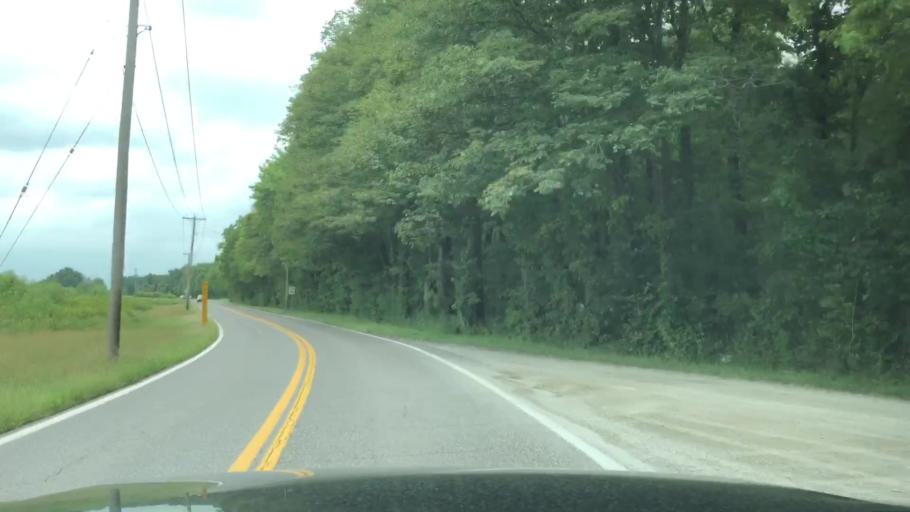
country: US
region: Missouri
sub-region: Saint Louis County
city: Bridgeton
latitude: 38.8111
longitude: -90.3958
